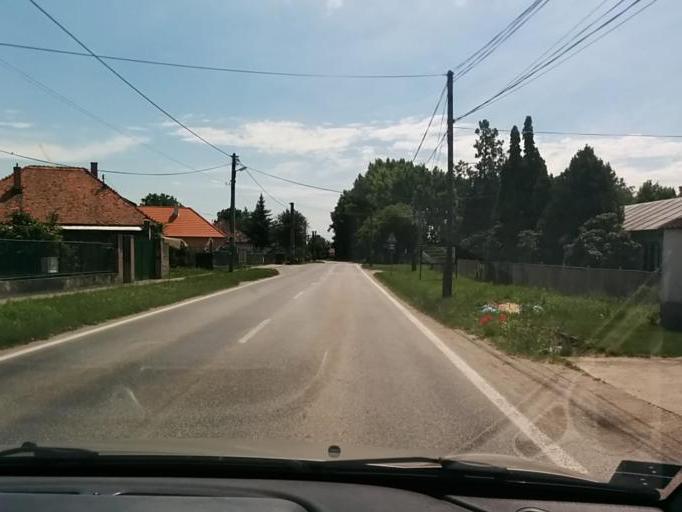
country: SK
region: Trnavsky
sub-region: Okres Galanta
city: Galanta
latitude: 48.2603
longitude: 17.8065
